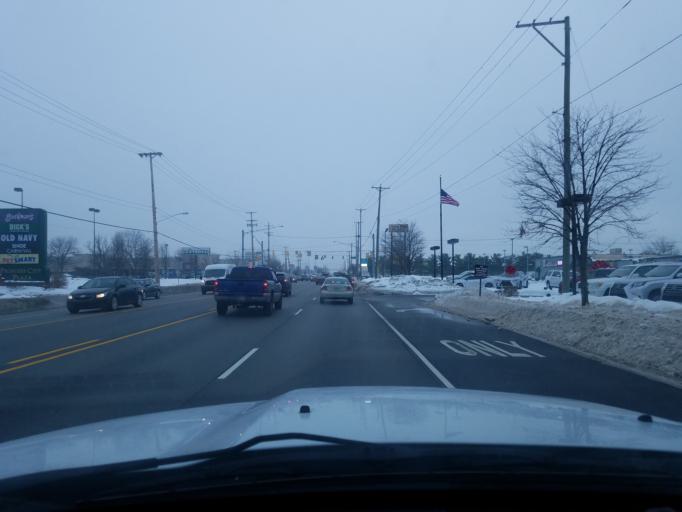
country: US
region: Indiana
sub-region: Saint Joseph County
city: Mishawaka
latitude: 41.6996
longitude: -86.1875
